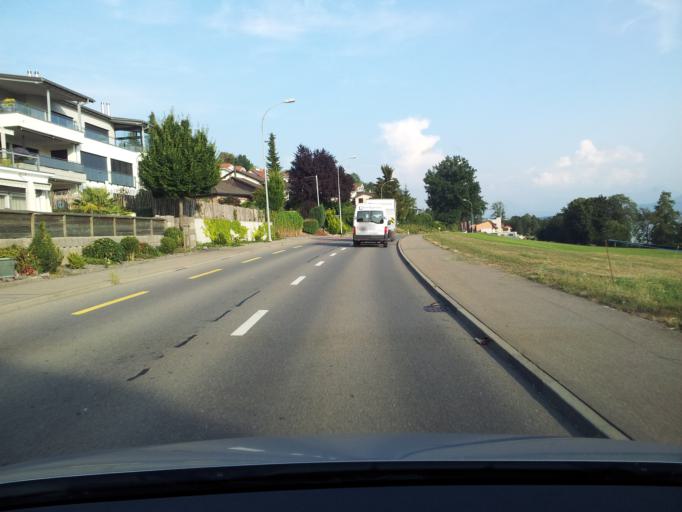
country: CH
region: Lucerne
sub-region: Sursee District
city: Eich
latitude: 47.1503
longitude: 8.1688
